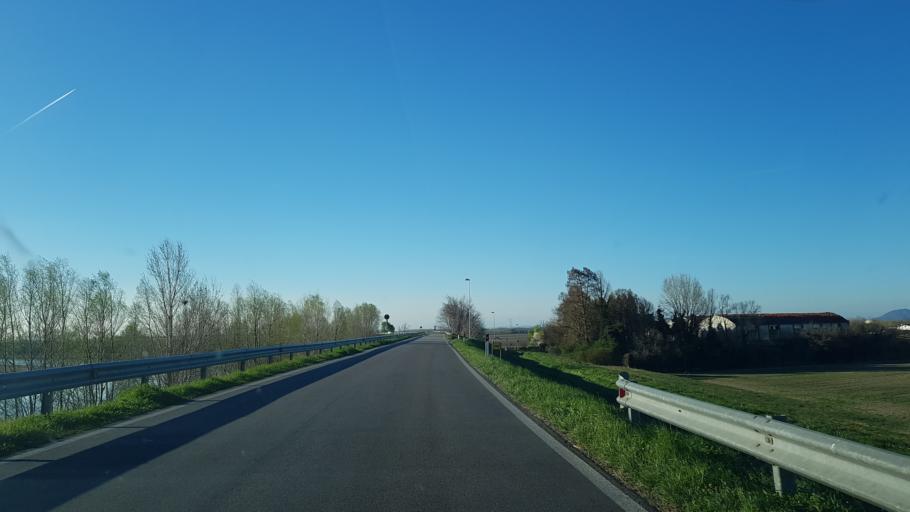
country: IT
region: Veneto
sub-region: Provincia di Rovigo
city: Lendinara
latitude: 45.1156
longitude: 11.6034
